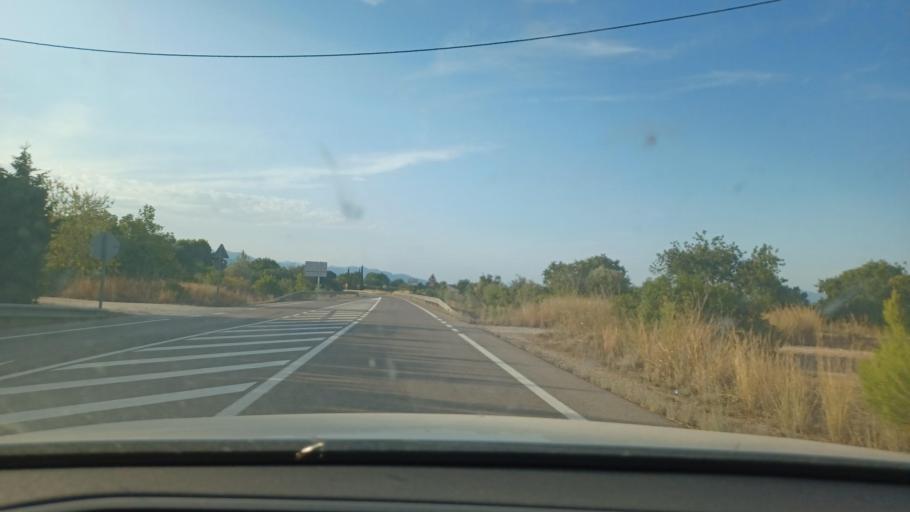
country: ES
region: Catalonia
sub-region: Provincia de Tarragona
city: Santa Barbara
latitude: 40.7116
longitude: 0.4849
